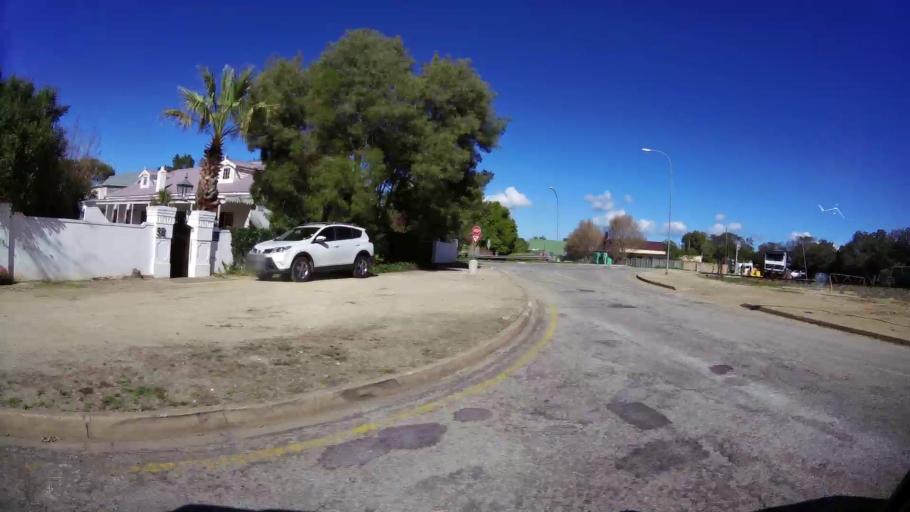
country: ZA
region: Western Cape
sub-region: Eden District Municipality
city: George
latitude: -33.9463
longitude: 22.4657
